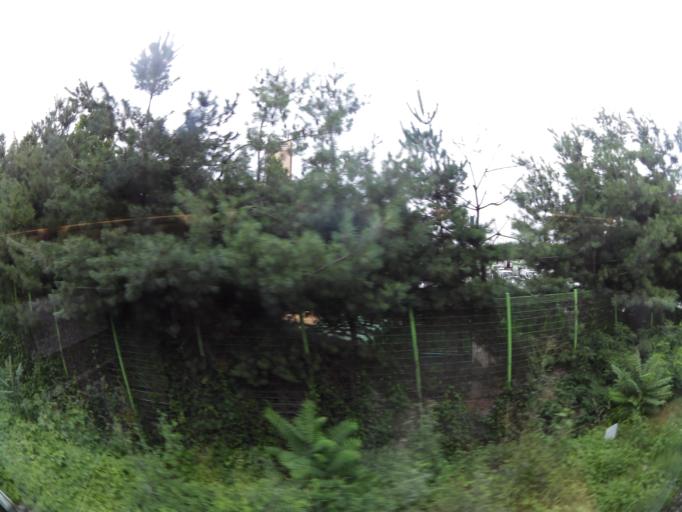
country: KR
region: Seoul
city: Seoul
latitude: 37.5155
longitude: 126.9467
